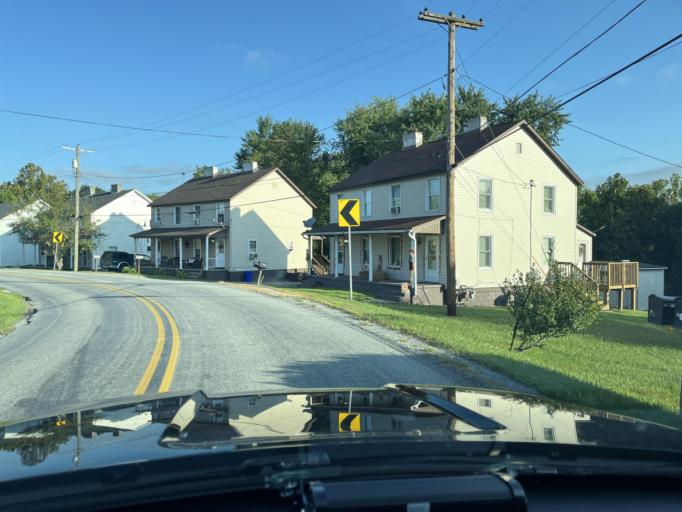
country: US
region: Pennsylvania
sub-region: Fayette County
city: Hopwood
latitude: 39.8771
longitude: -79.7162
